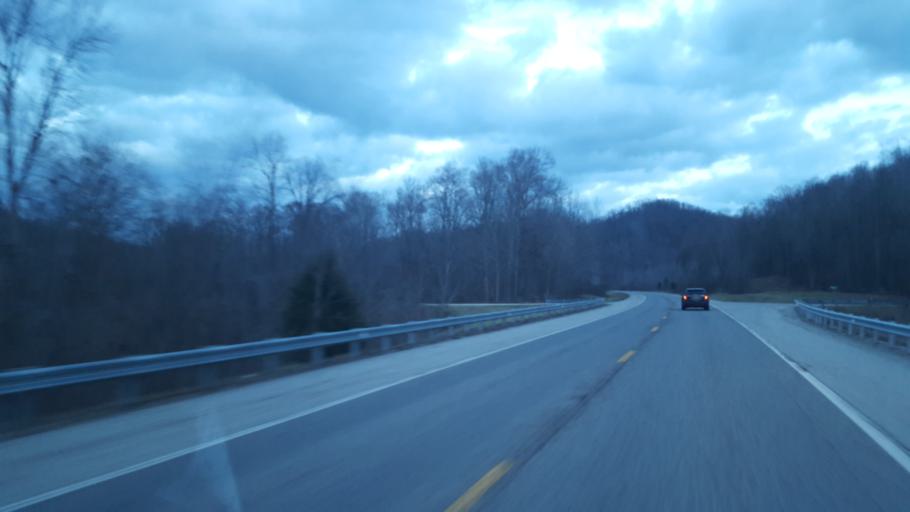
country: US
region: Kentucky
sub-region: Lewis County
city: Vanceburg
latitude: 38.5943
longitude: -83.1867
